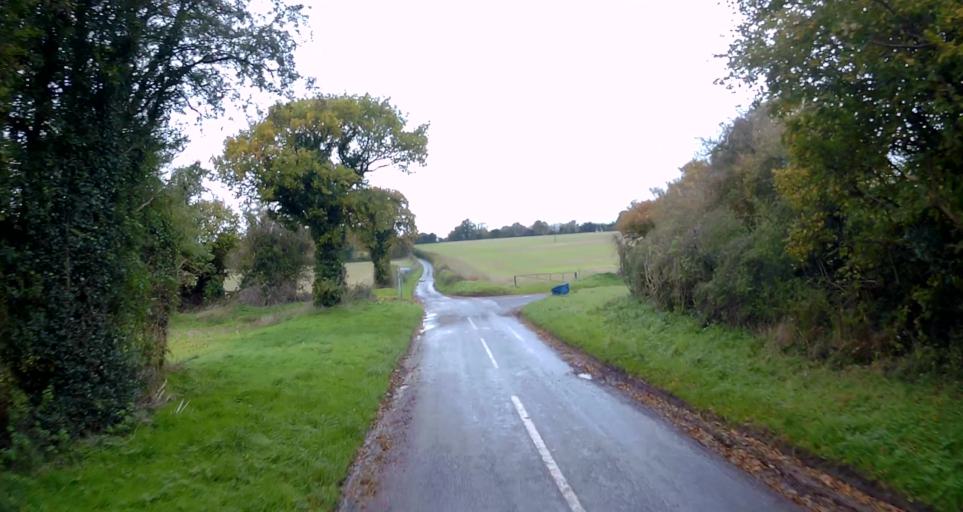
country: GB
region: England
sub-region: Hampshire
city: Four Marks
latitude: 51.1533
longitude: -1.0841
